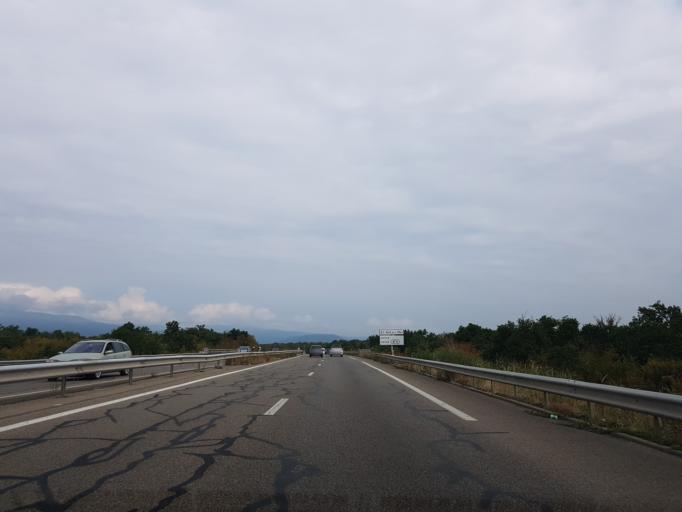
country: FR
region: Alsace
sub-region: Departement du Haut-Rhin
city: Pulversheim
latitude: 47.8135
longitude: 7.2987
